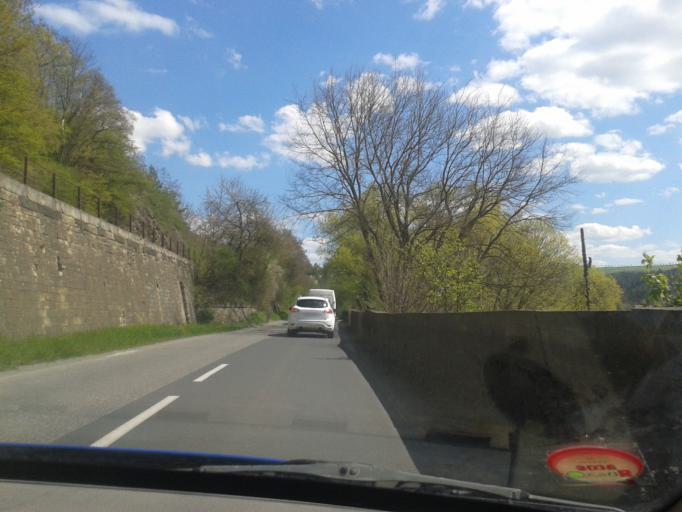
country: CZ
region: Central Bohemia
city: Nizbor
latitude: 49.9976
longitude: 14.0205
